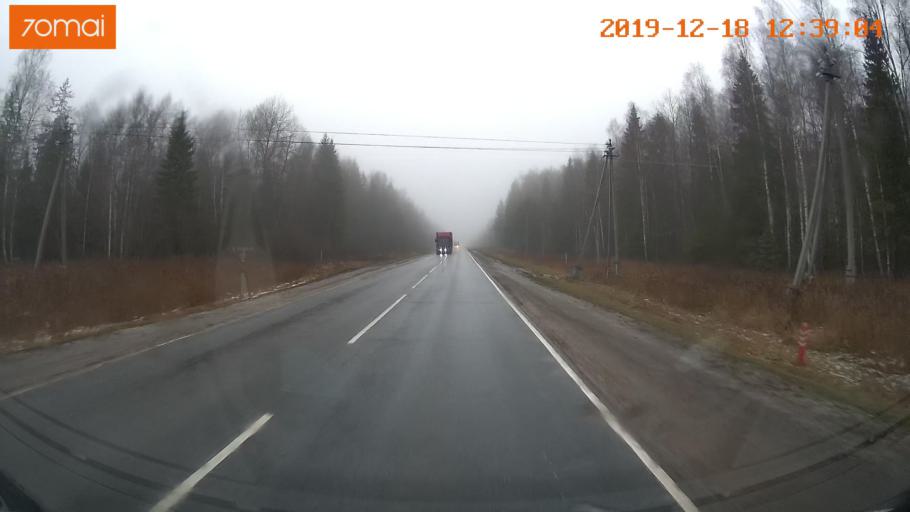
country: RU
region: Moskovskaya
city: Vysokovsk
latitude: 56.1599
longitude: 36.6090
